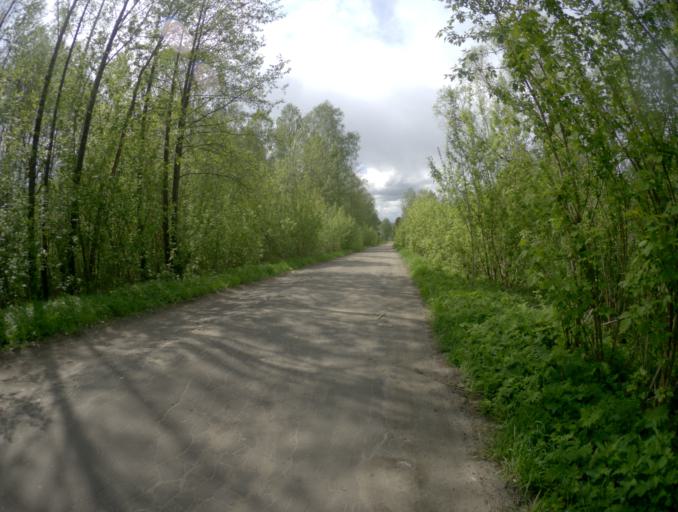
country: RU
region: Vladimir
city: Velikodvorskiy
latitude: 55.2408
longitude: 40.6676
